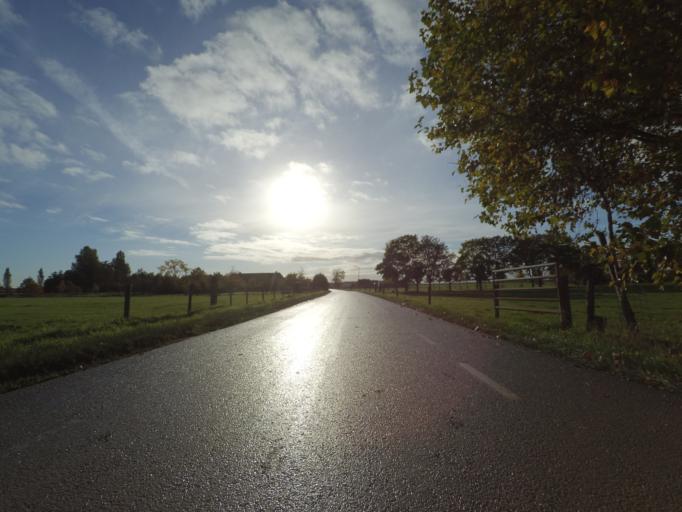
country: NL
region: Utrecht
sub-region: Gemeente Utrechtse Heuvelrug
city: Driebergen-Rijsenburg
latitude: 52.0151
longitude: 5.2572
